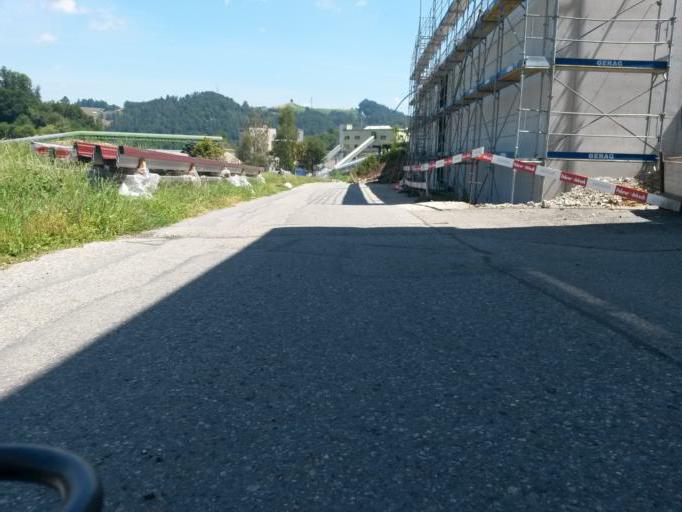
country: CH
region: Bern
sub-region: Emmental District
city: Lutzelfluh
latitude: 47.0084
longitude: 7.6545
